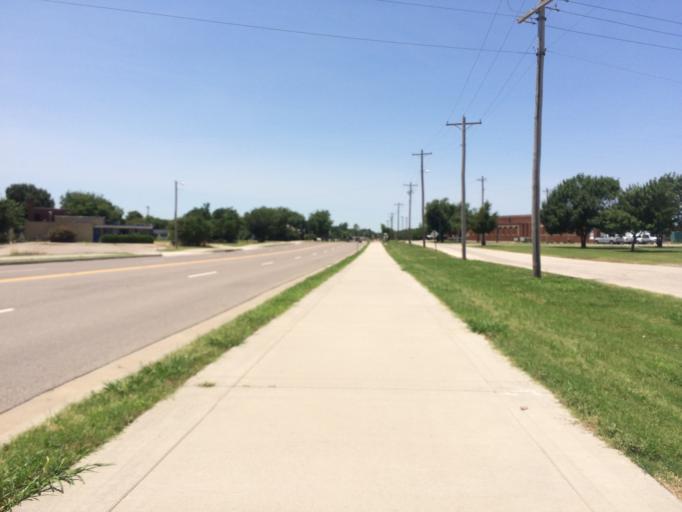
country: US
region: Oklahoma
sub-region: Cleveland County
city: Norman
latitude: 35.2258
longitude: -97.4268
